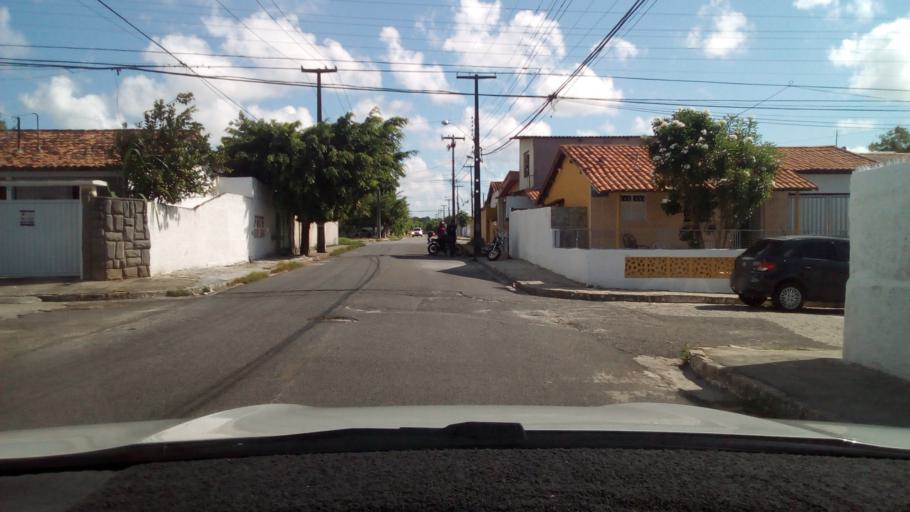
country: BR
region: Paraiba
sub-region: Joao Pessoa
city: Joao Pessoa
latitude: -7.1318
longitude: -34.8504
